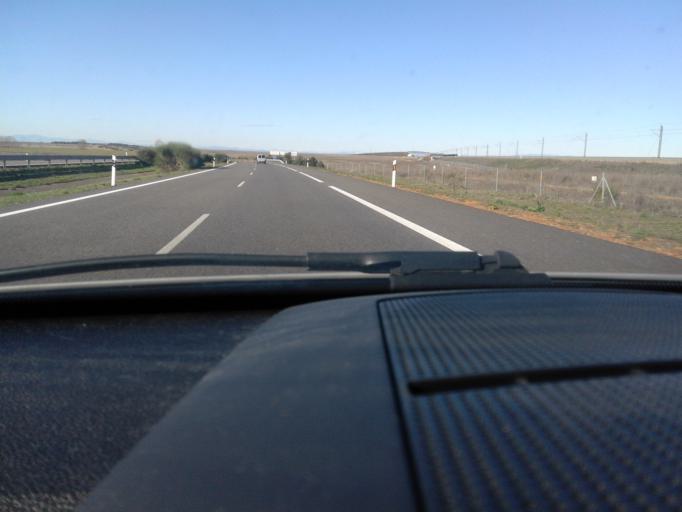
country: ES
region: Castille and Leon
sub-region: Provincia de Leon
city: Villamoratiel de las Matas
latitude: 42.4206
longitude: -5.2411
